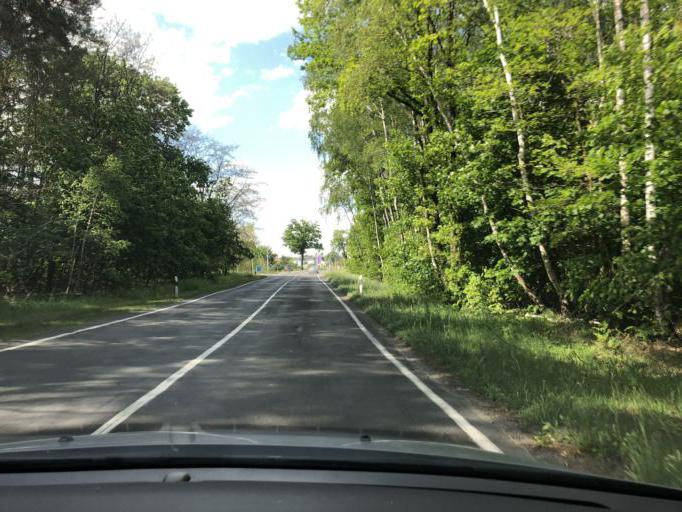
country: DE
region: Brandenburg
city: Spreenhagen
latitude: 52.3233
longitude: 13.9012
